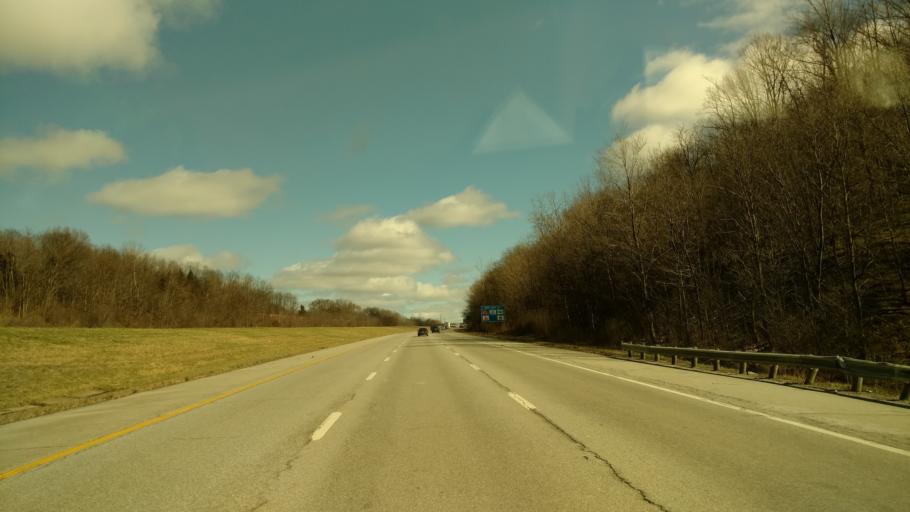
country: US
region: Ohio
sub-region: Lake County
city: Willoughby
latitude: 41.6313
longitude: -81.3924
